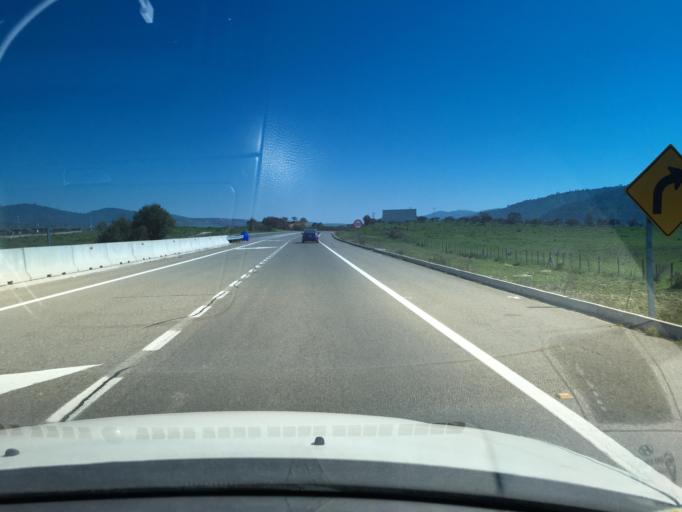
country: CL
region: Valparaiso
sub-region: San Antonio Province
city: El Tabo
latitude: -33.3905
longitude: -71.4423
